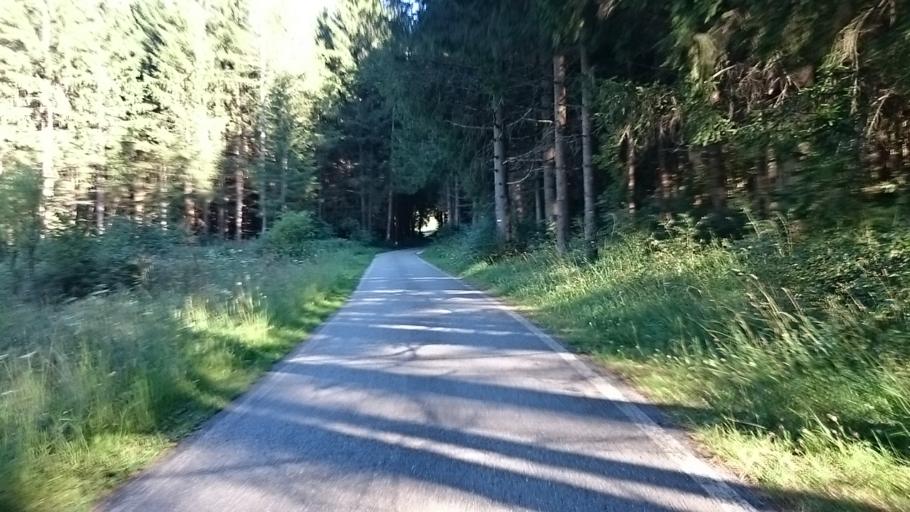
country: IT
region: Trentino-Alto Adige
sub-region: Bolzano
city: Braies
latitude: 46.7404
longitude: 12.1291
